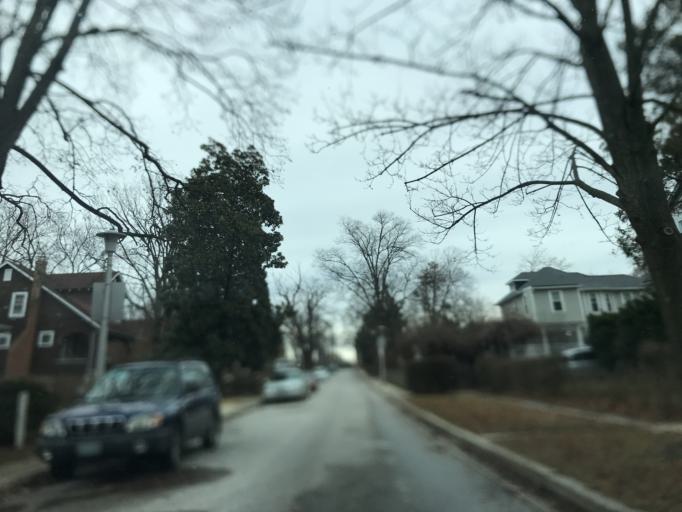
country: US
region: Maryland
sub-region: Baltimore County
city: Towson
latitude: 39.3499
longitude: -76.6129
